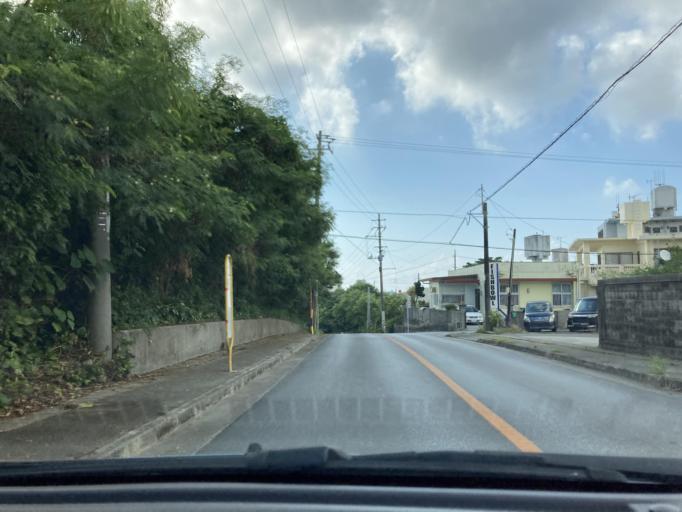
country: JP
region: Okinawa
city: Itoman
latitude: 26.1344
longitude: 127.7702
